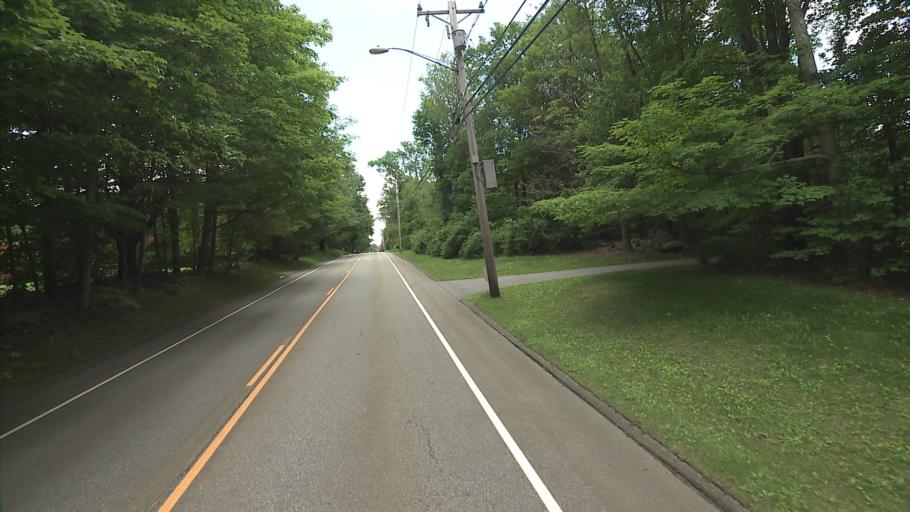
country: US
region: Connecticut
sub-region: Litchfield County
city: West Torrington
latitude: 41.8405
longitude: -73.2333
